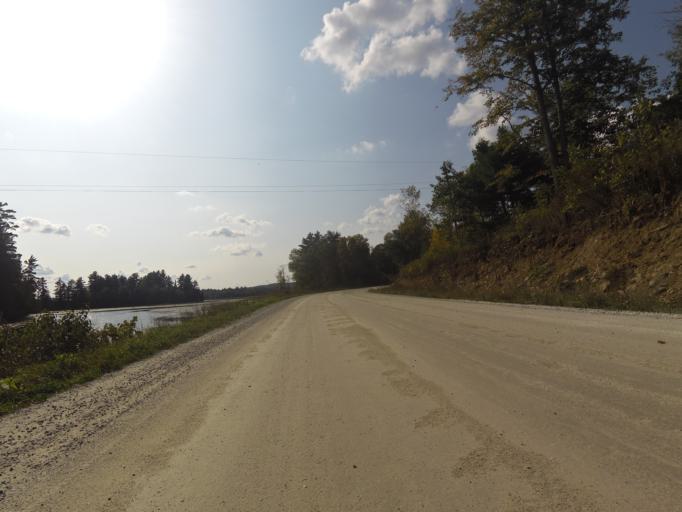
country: CA
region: Ontario
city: Renfrew
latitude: 45.1350
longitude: -76.6587
